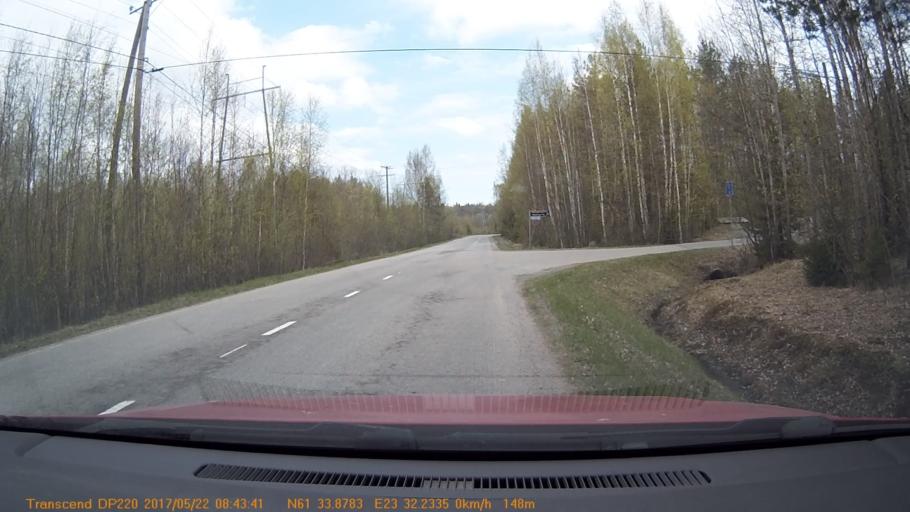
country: FI
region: Pirkanmaa
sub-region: Tampere
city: Yloejaervi
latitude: 61.5646
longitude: 23.5372
